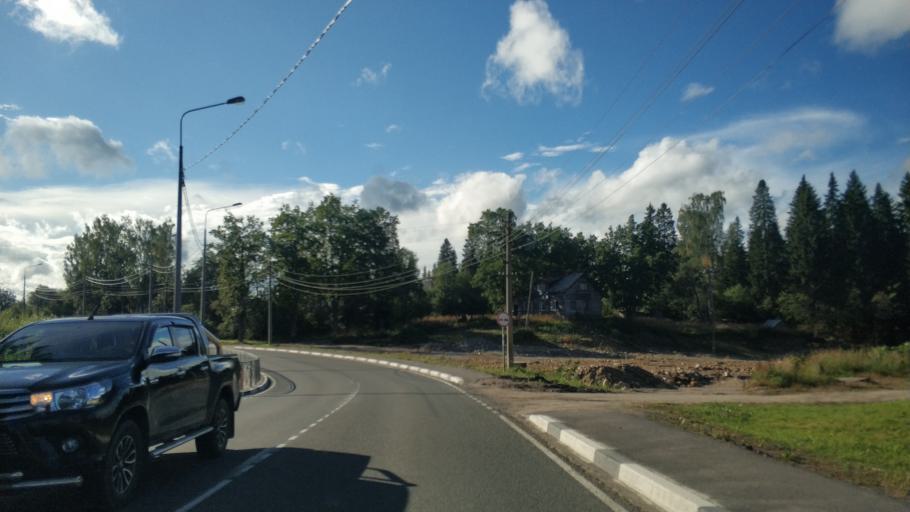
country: RU
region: Republic of Karelia
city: Lakhdenpokh'ya
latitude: 61.5229
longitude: 30.1836
